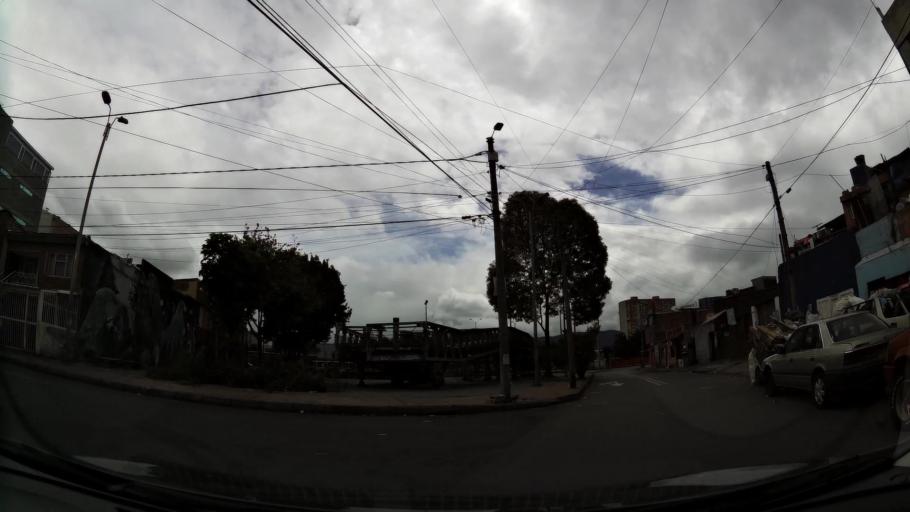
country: CO
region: Bogota D.C.
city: Barrio San Luis
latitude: 4.6903
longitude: -74.0851
